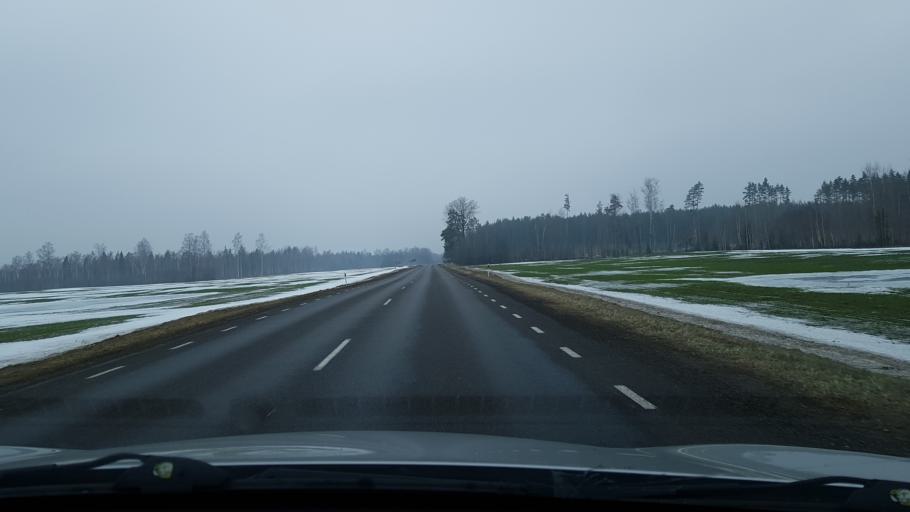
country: EE
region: Valgamaa
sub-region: Torva linn
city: Torva
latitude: 58.1094
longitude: 26.0049
